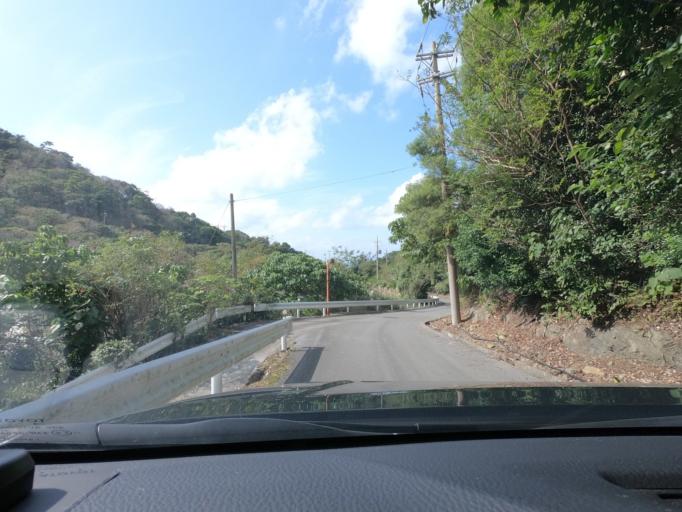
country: JP
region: Okinawa
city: Nago
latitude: 26.7570
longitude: 128.1937
